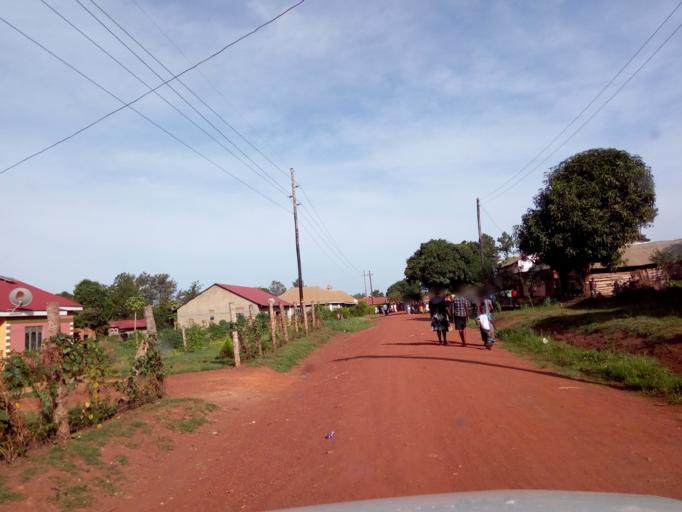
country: UG
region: Western Region
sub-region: Masindi District
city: Masindi
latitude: 1.6788
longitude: 31.7211
